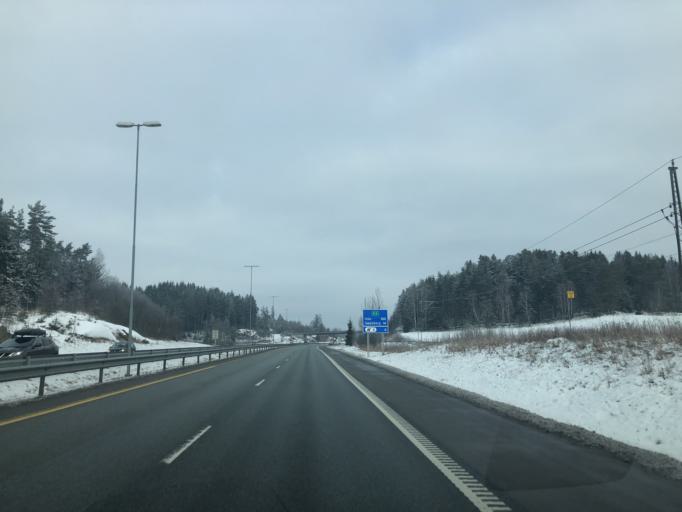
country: NO
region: Ostfold
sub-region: Sarpsborg
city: Skjeberg
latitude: 59.1858
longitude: 11.2010
